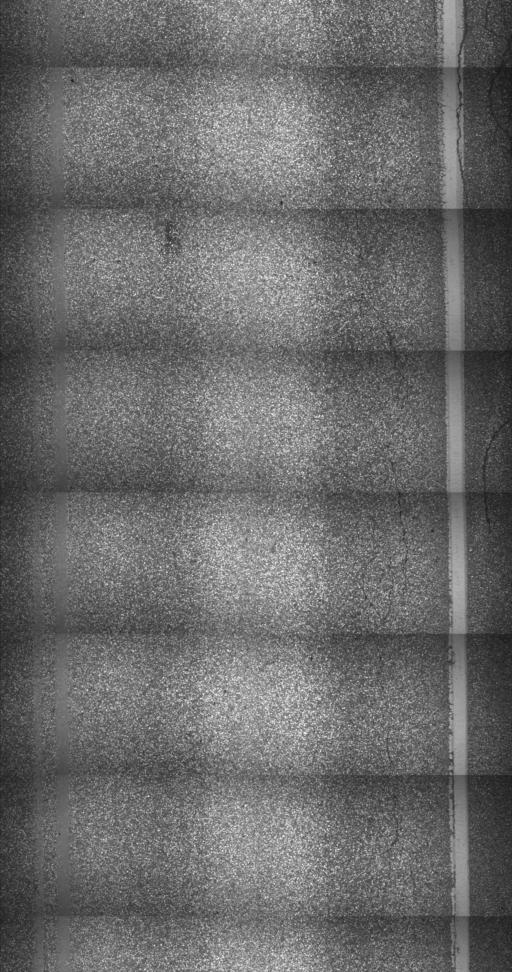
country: US
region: Vermont
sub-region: Rutland County
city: Castleton
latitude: 43.5906
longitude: -73.2100
